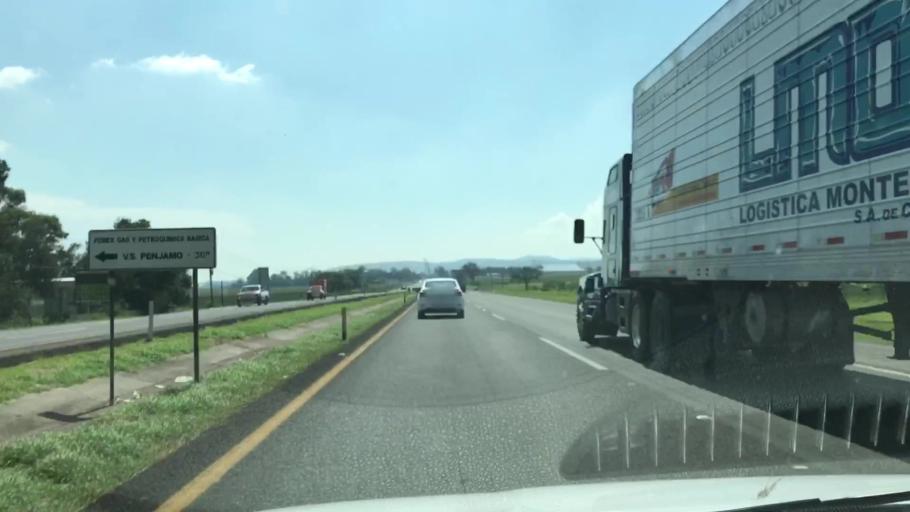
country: MX
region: Guanajuato
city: Penjamo
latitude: 20.4379
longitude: -101.6808
